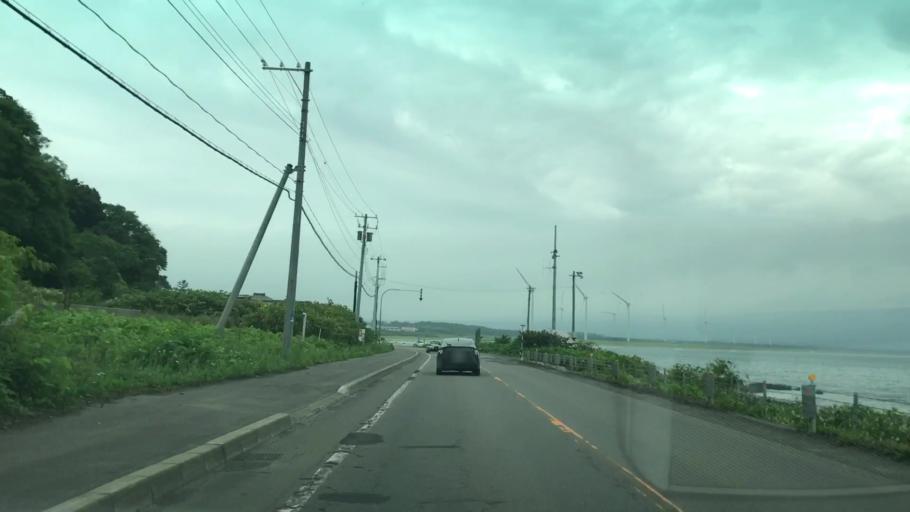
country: JP
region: Hokkaido
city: Iwanai
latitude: 42.7832
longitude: 140.3078
